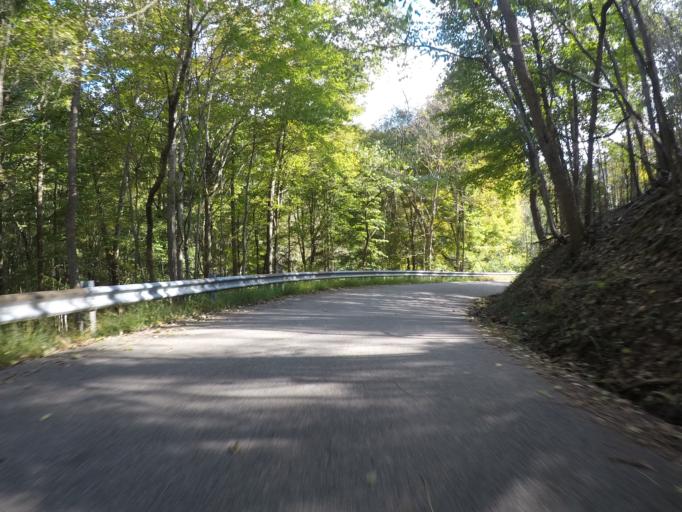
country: US
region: West Virginia
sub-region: Wayne County
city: Lavalette
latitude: 38.3668
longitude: -82.4791
